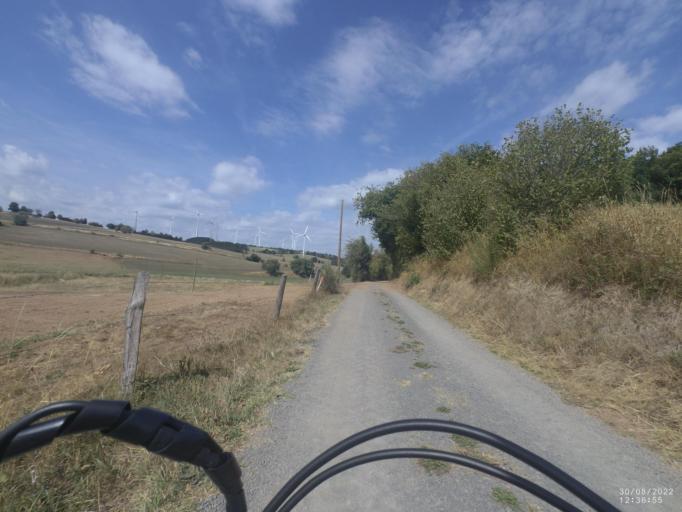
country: DE
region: Rheinland-Pfalz
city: Ormont
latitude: 50.3356
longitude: 6.4514
